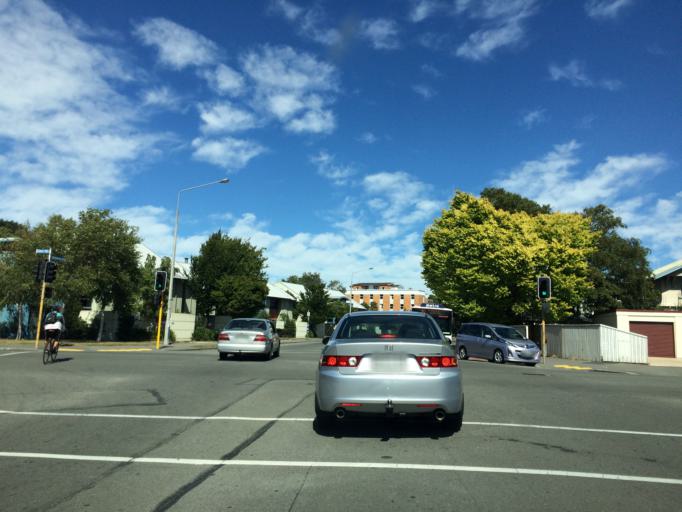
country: NZ
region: Canterbury
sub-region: Christchurch City
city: Christchurch
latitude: -43.5197
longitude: 172.5792
